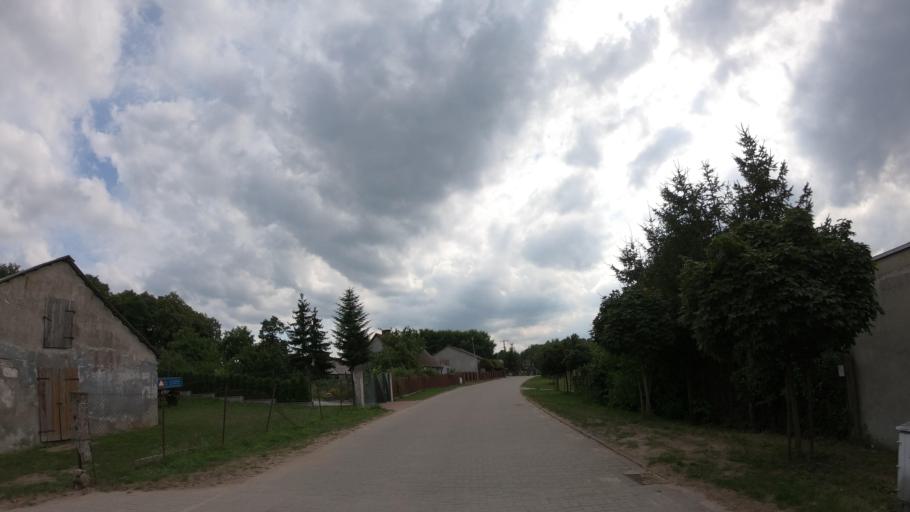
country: PL
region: West Pomeranian Voivodeship
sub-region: Powiat drawski
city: Kalisz Pomorski
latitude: 53.2964
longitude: 15.9168
